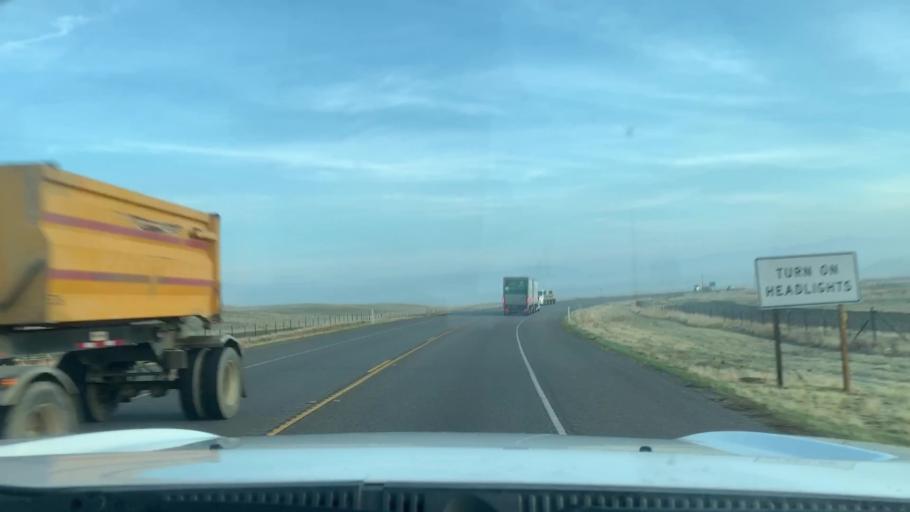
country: US
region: California
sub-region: San Luis Obispo County
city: Shandon
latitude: 35.7302
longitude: -120.2931
